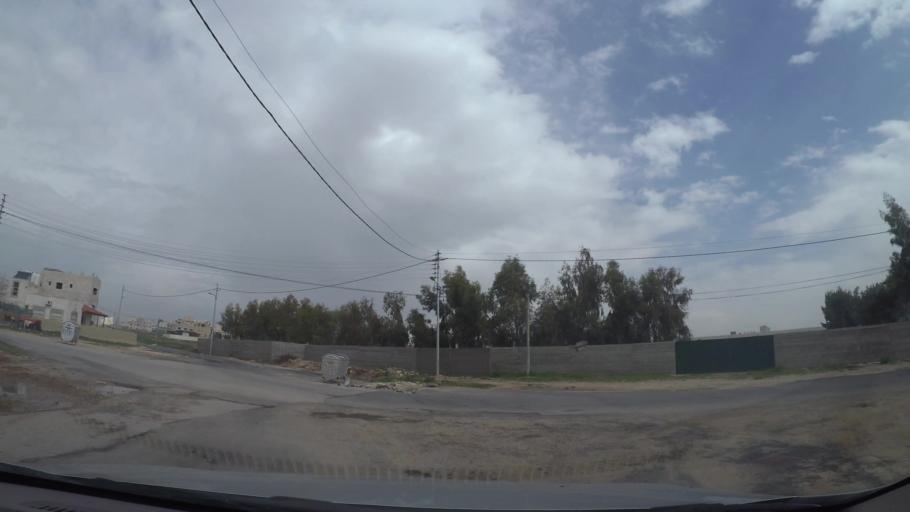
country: JO
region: Amman
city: Umm as Summaq
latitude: 31.9107
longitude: 35.8511
